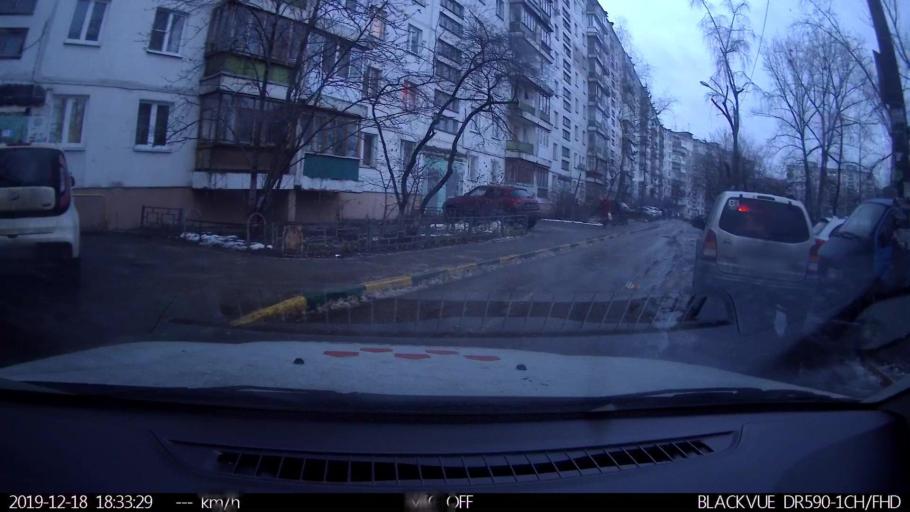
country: RU
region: Nizjnij Novgorod
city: Nizhniy Novgorod
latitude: 56.3315
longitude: 43.9431
